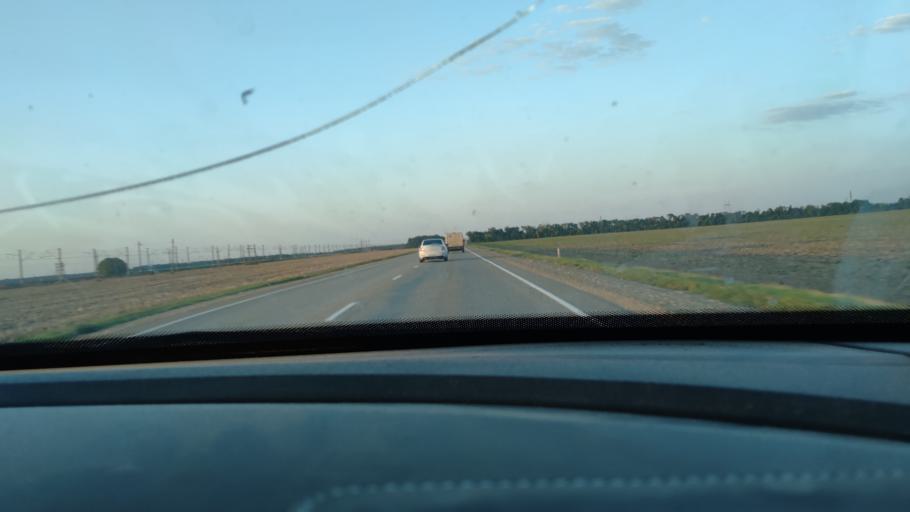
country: RU
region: Krasnodarskiy
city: Novominskaya
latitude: 46.3865
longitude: 38.9867
